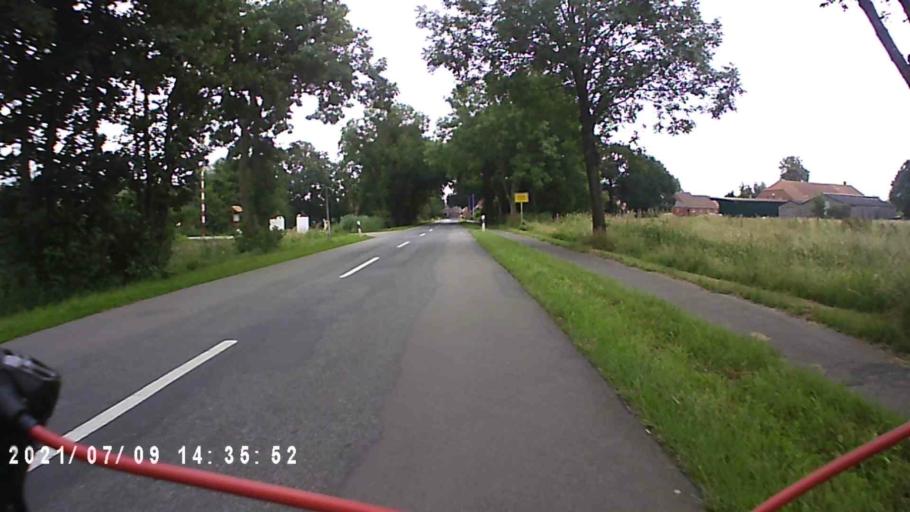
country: DE
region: Lower Saxony
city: Weener
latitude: 53.1149
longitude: 7.3319
